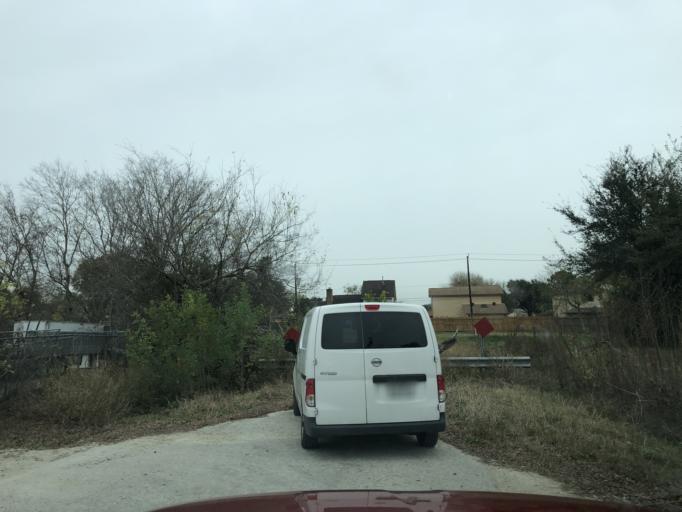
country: US
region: Texas
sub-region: Fort Bend County
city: Missouri City
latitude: 29.6377
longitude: -95.5225
